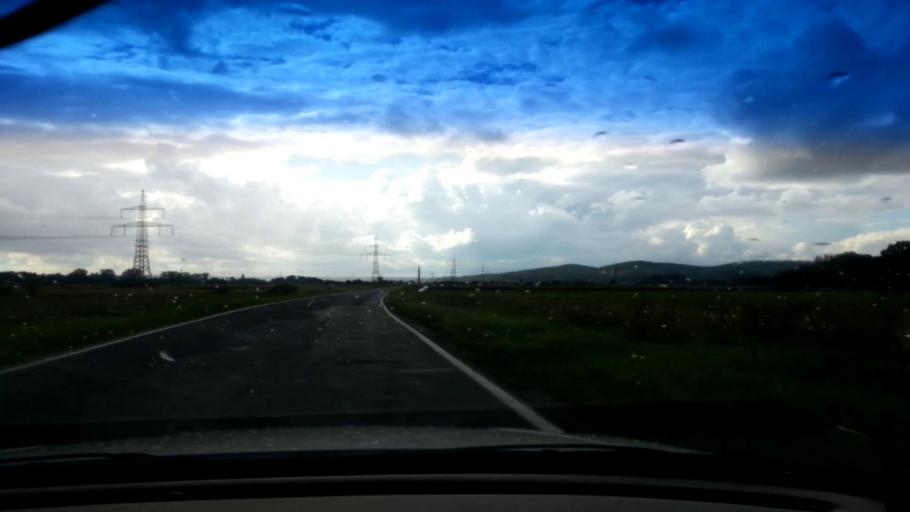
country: DE
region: Bavaria
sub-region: Upper Franconia
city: Gundelsheim
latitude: 49.9357
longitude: 10.9055
